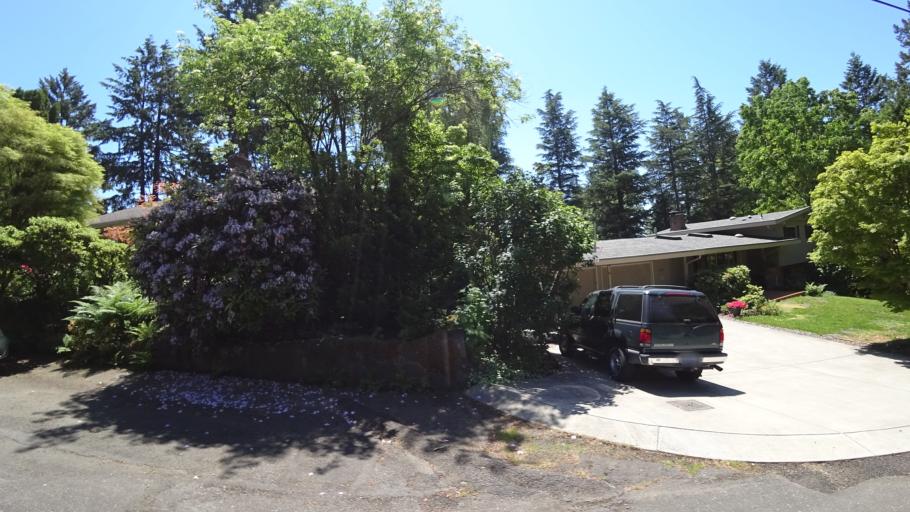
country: US
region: Oregon
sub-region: Washington County
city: Raleigh Hills
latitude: 45.4928
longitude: -122.7172
